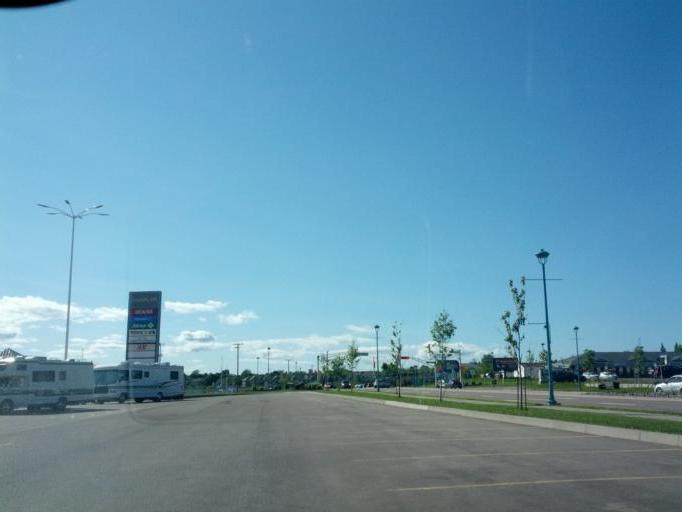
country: CA
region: New Brunswick
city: Moncton
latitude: 46.0979
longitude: -64.7592
